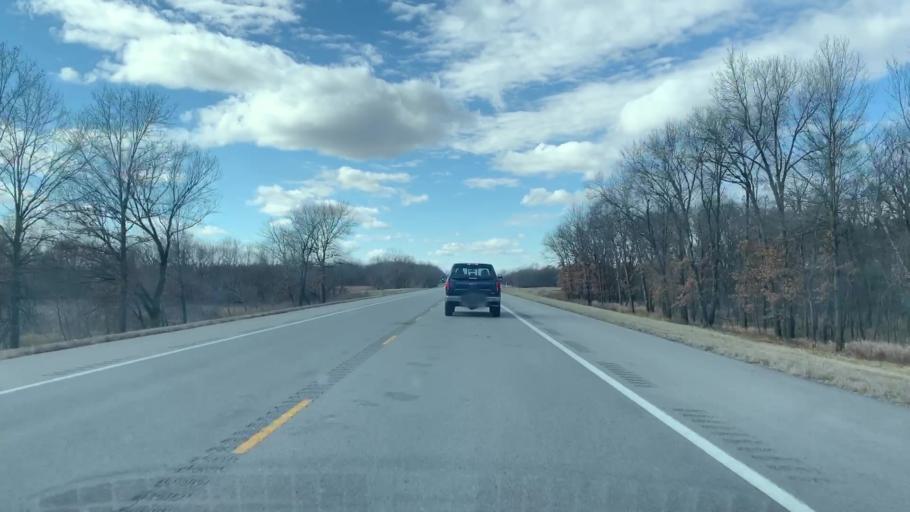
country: US
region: Kansas
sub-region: Cherokee County
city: Columbus
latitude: 37.3401
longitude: -94.9750
